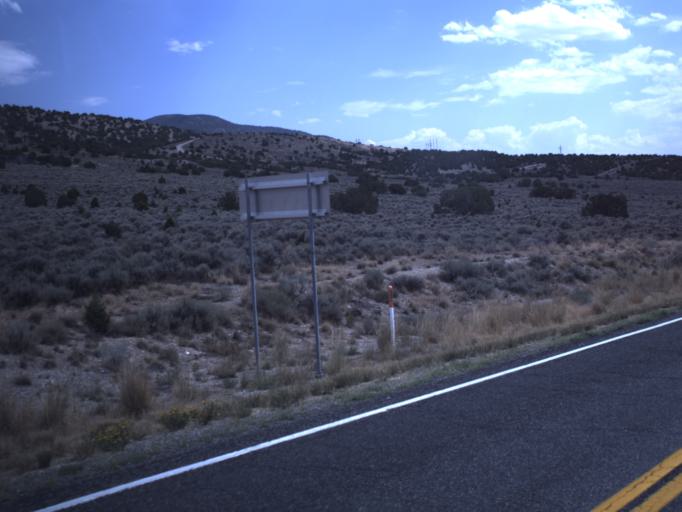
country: US
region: Utah
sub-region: Tooele County
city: Tooele
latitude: 40.3240
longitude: -112.2880
